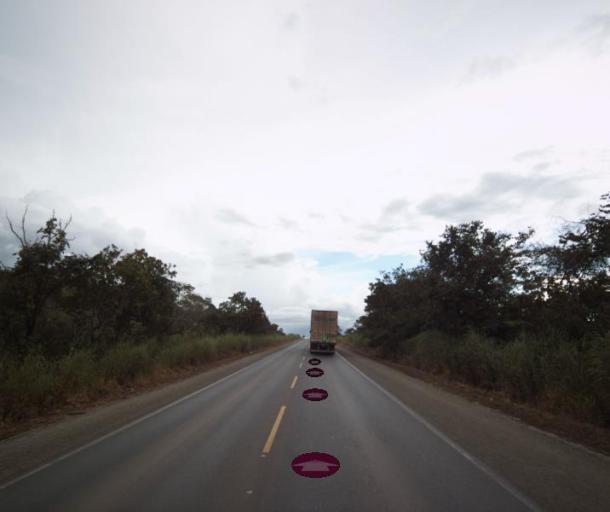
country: BR
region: Goias
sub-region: Itapaci
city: Itapaci
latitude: -14.9351
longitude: -49.3683
